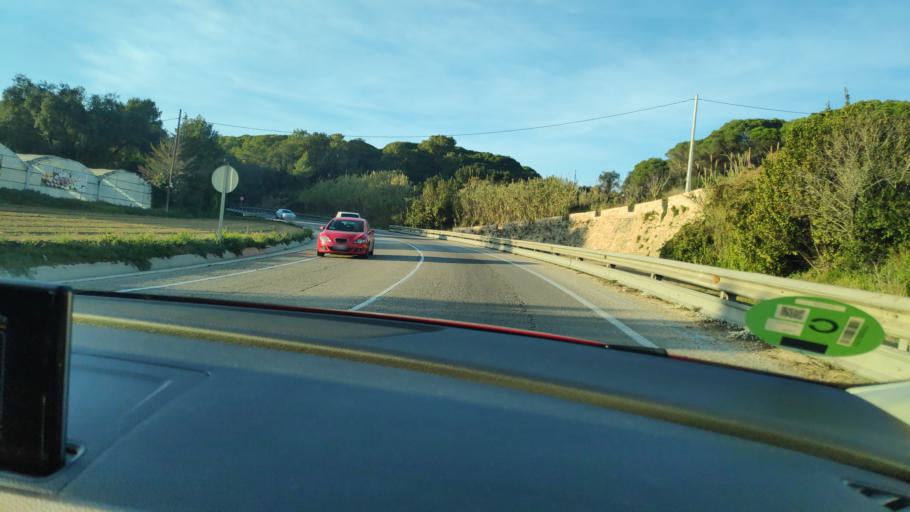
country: ES
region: Catalonia
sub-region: Provincia de Girona
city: Lloret de Mar
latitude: 41.7174
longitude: 2.8290
